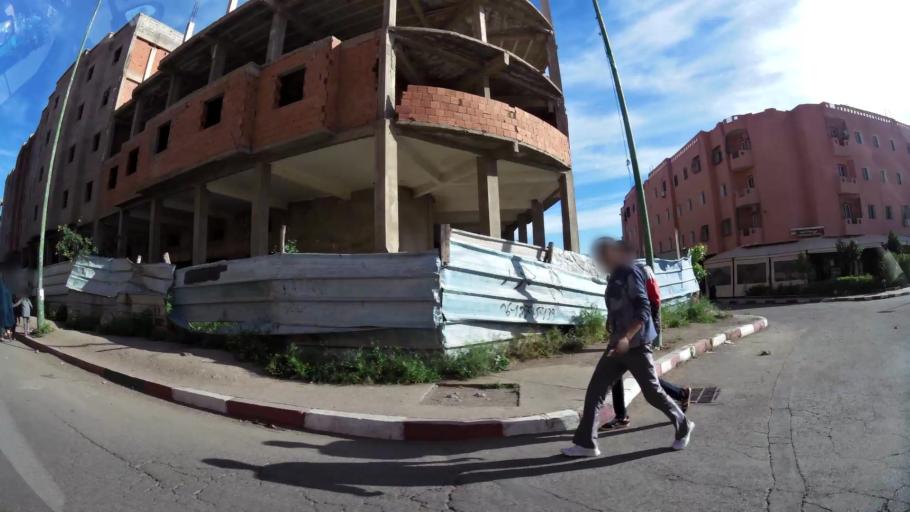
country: MA
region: Marrakech-Tensift-Al Haouz
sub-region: Marrakech
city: Marrakesh
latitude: 31.6862
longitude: -8.0650
